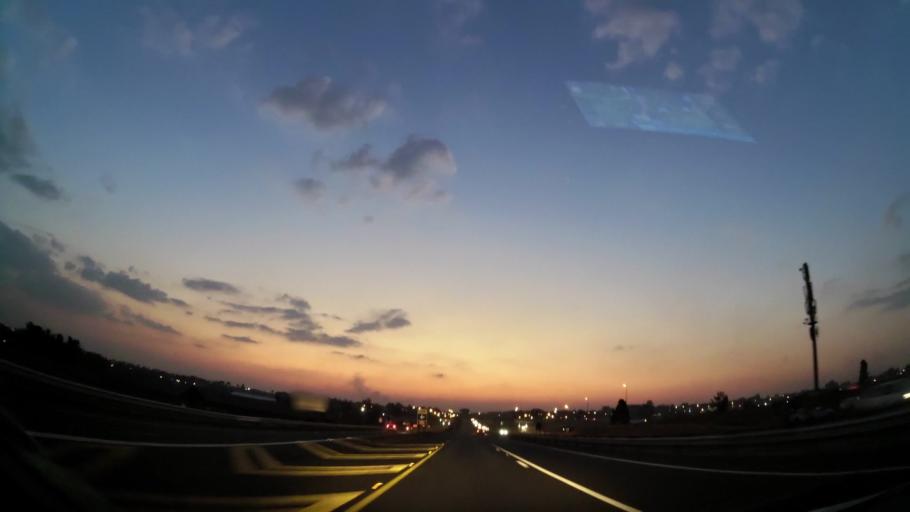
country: ZA
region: Gauteng
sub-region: Ekurhuleni Metropolitan Municipality
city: Brakpan
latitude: -26.2691
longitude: 28.3643
